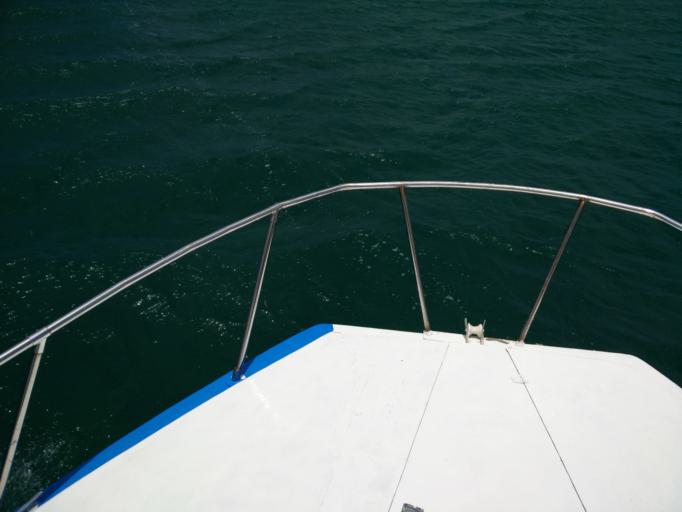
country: GP
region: Guadeloupe
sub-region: Guadeloupe
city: Petit-Canal
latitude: 16.3804
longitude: -61.5043
